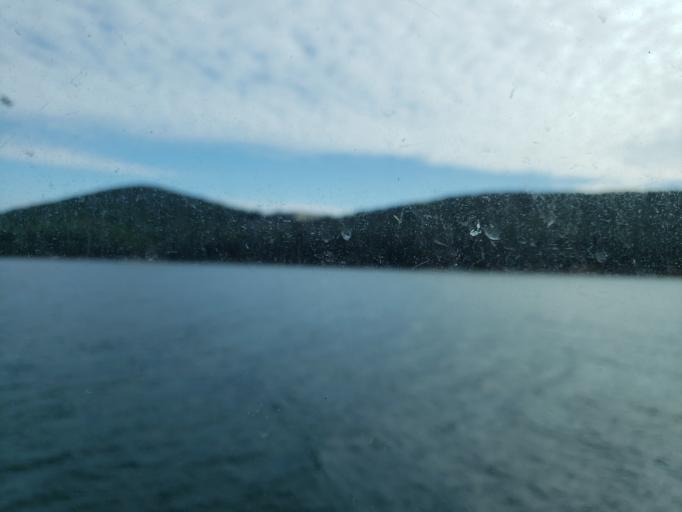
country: TR
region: Istanbul
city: Adalan
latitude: 40.8800
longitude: 29.0789
